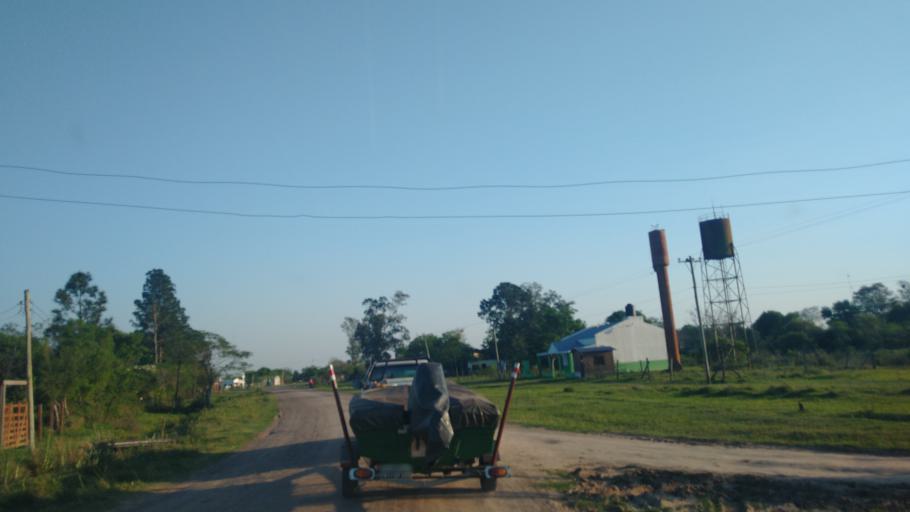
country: PY
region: Neembucu
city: Cerrito
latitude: -27.3752
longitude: -57.6548
